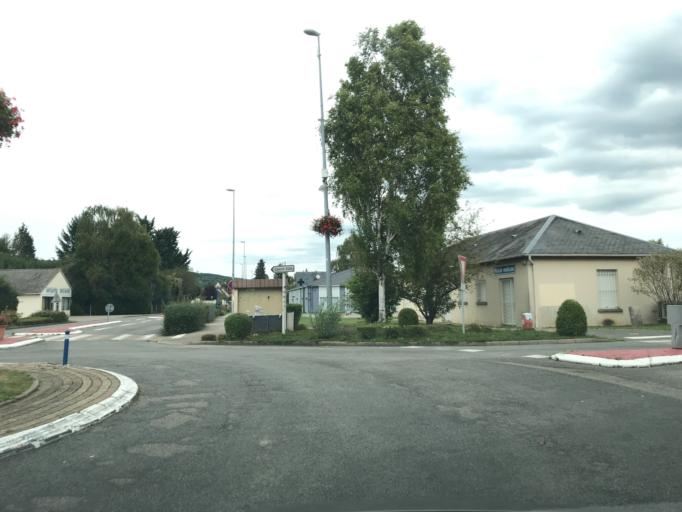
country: FR
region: Haute-Normandie
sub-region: Departement de l'Eure
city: Aubevoye
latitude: 49.1672
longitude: 1.3365
